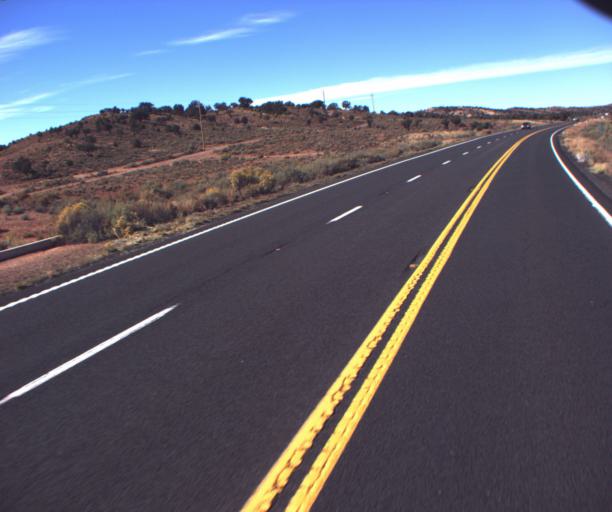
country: US
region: Arizona
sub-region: Coconino County
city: Tuba City
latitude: 36.4007
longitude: -111.5318
